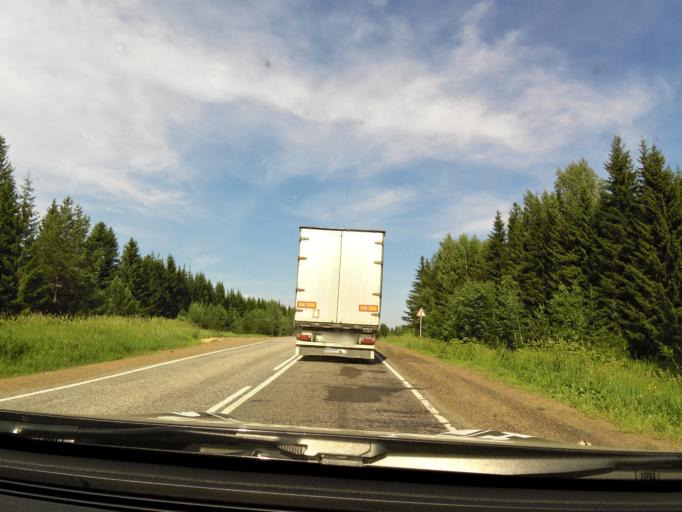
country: RU
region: Kirov
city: Belaya Kholunitsa
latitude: 58.8157
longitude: 50.5904
